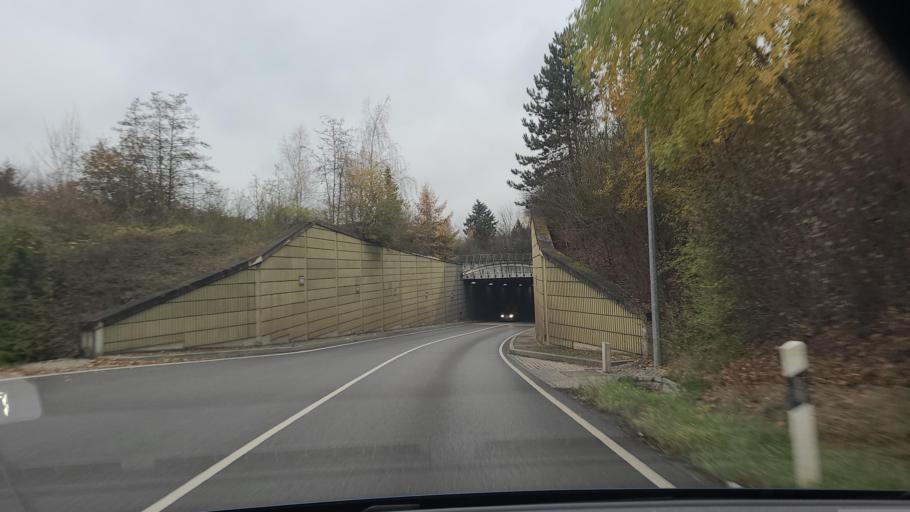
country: LU
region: Luxembourg
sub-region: Canton de Luxembourg
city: Bertrange
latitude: 49.6190
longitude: 6.0531
